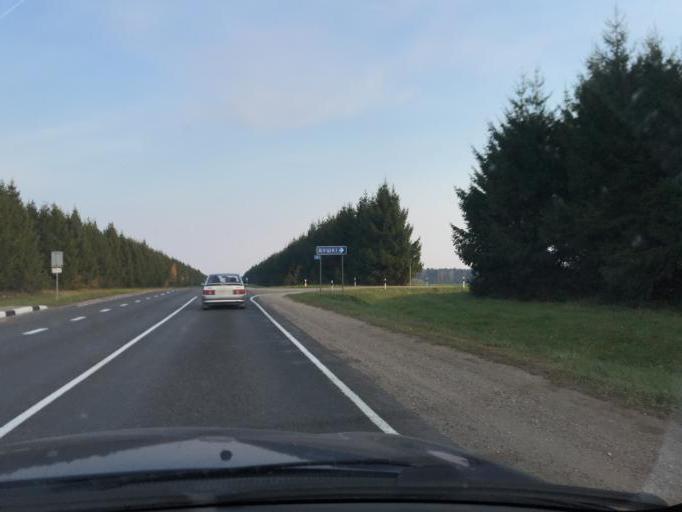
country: BY
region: Grodnenskaya
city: Karelichy
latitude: 53.5922
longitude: 26.0826
